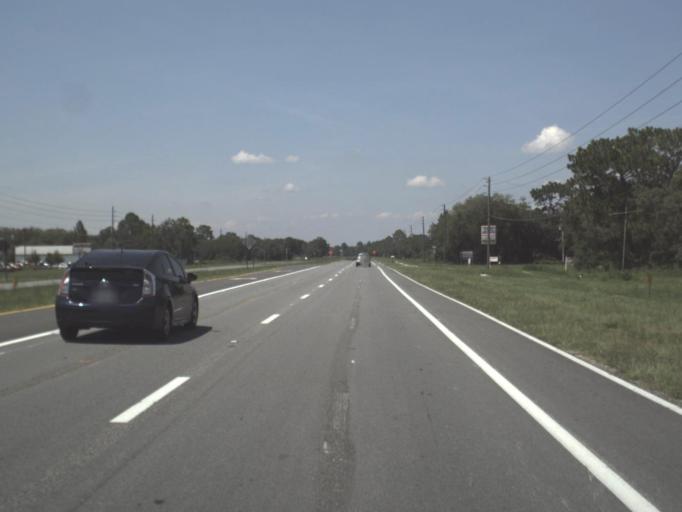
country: US
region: Florida
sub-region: Hernando County
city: North Weeki Wachee
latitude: 28.5870
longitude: -82.5539
